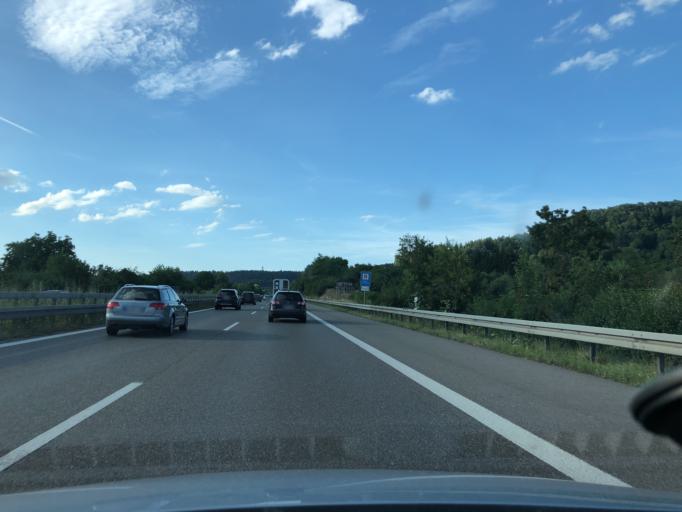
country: DE
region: Baden-Wuerttemberg
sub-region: Regierungsbezirk Stuttgart
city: Herrenberg
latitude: 48.5874
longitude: 8.8981
